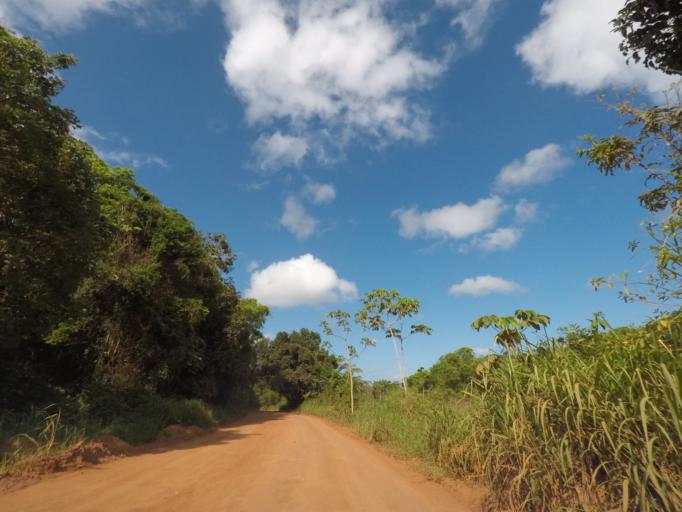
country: BR
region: Bahia
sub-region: Itacare
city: Itacare
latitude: -14.2146
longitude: -39.0582
